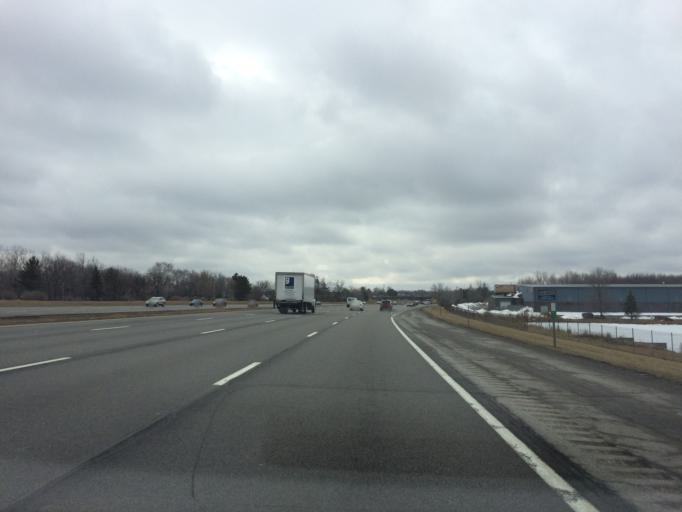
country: US
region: New York
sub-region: Monroe County
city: Rochester
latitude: 43.1006
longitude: -77.6008
